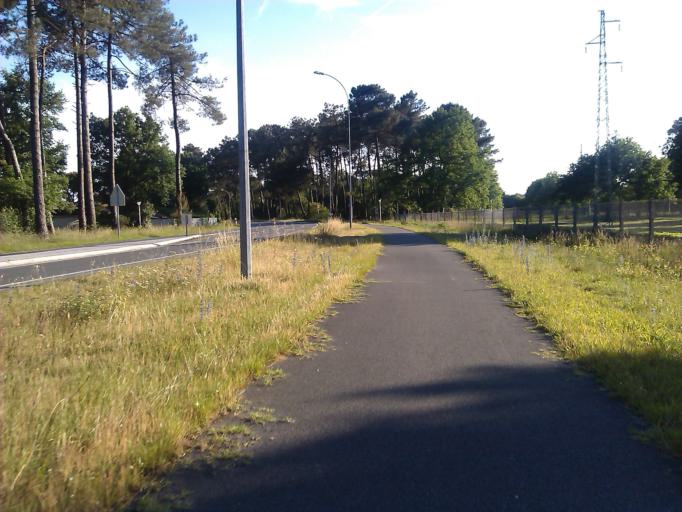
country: FR
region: Aquitaine
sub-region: Departement de la Gironde
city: Cestas
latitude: 44.7734
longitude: -0.6918
